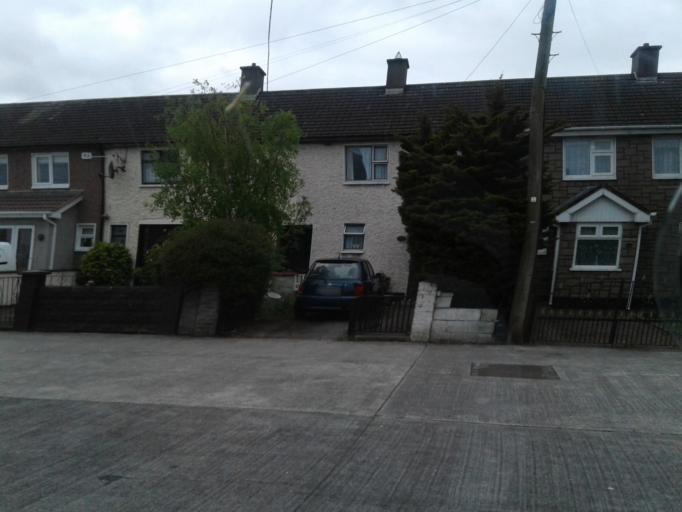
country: IE
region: Leinster
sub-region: Dublin City
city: Finglas
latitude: 53.3913
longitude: -6.3116
